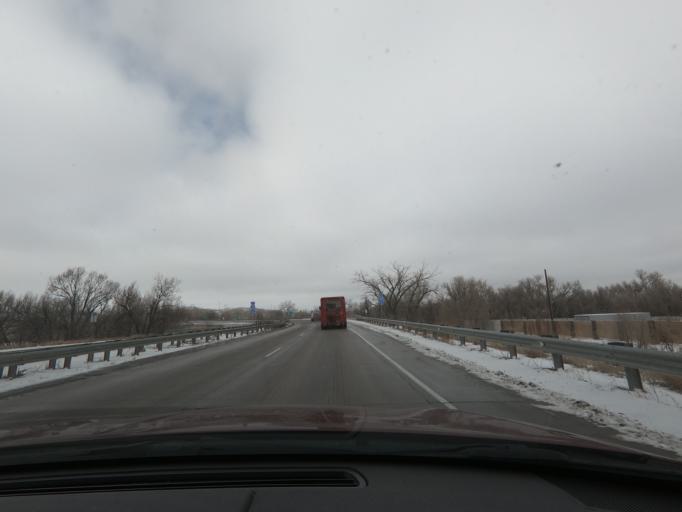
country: US
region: Colorado
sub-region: El Paso County
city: Security-Widefield
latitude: 38.7254
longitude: -104.7267
